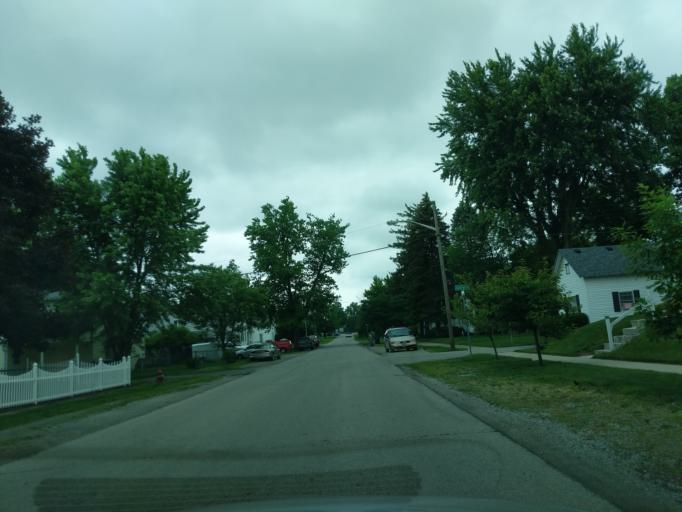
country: US
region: Indiana
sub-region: Hamilton County
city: Cicero
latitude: 40.1288
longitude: -86.0161
